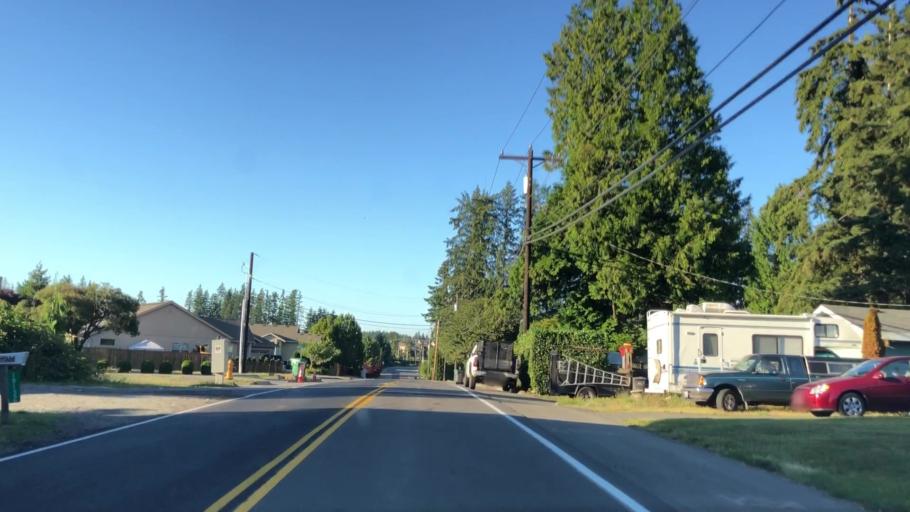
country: US
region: Washington
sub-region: Snohomish County
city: North Creek
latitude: 47.8233
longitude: -122.1894
